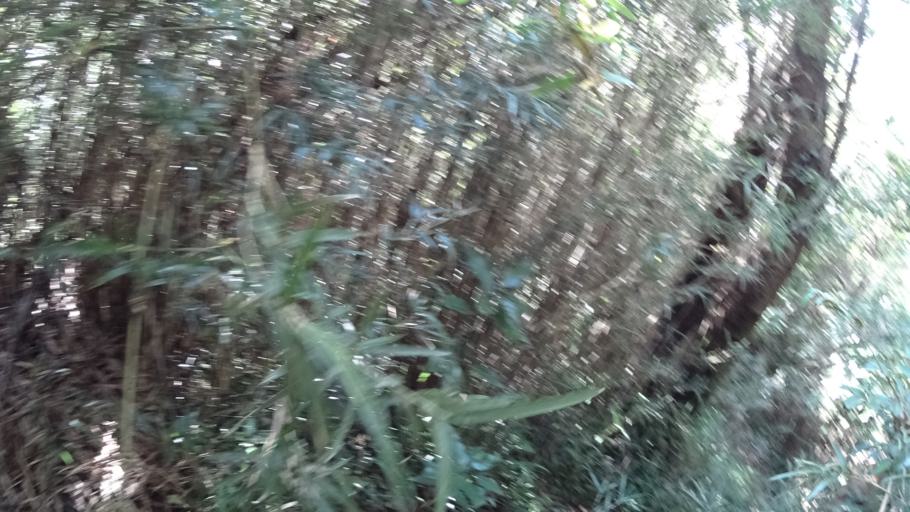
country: JP
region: Kanagawa
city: Hayama
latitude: 35.2764
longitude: 139.6170
